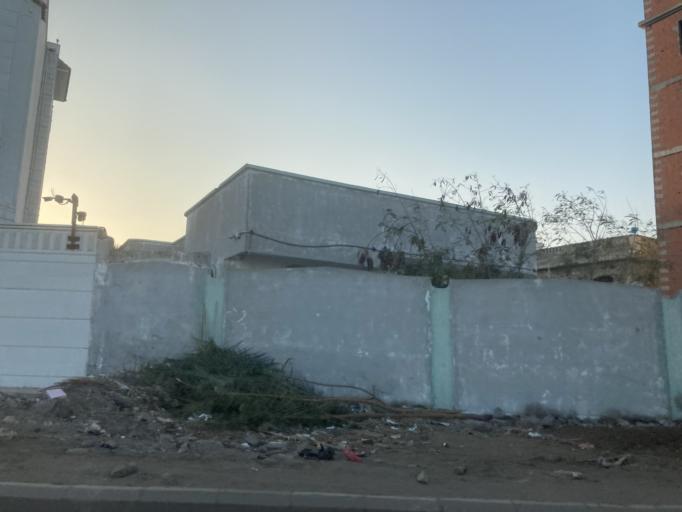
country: YE
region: Aden
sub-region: Al Mansura
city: Al Mansurah
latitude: 12.8535
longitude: 44.9915
